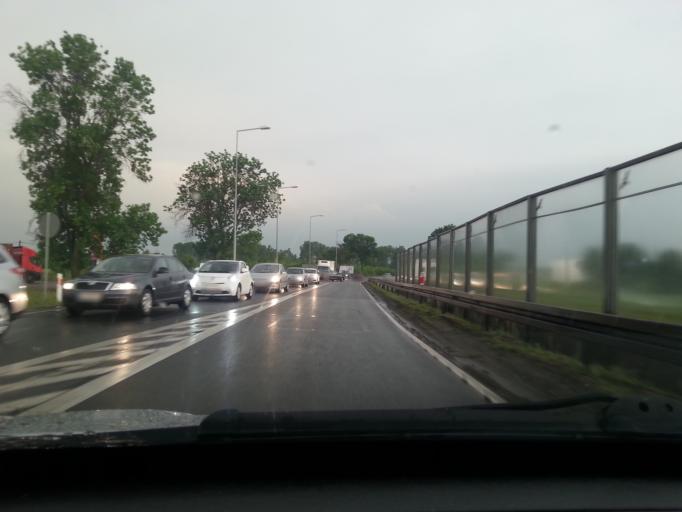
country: PL
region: Lodz Voivodeship
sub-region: Powiat zgierski
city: Strykow
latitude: 51.8825
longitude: 19.5826
